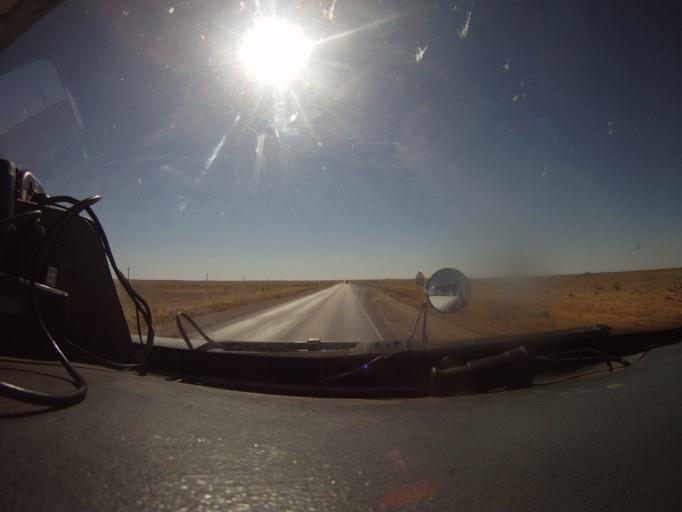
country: KZ
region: Qyzylorda
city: Zhosaly
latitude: 45.5917
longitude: 63.9599
